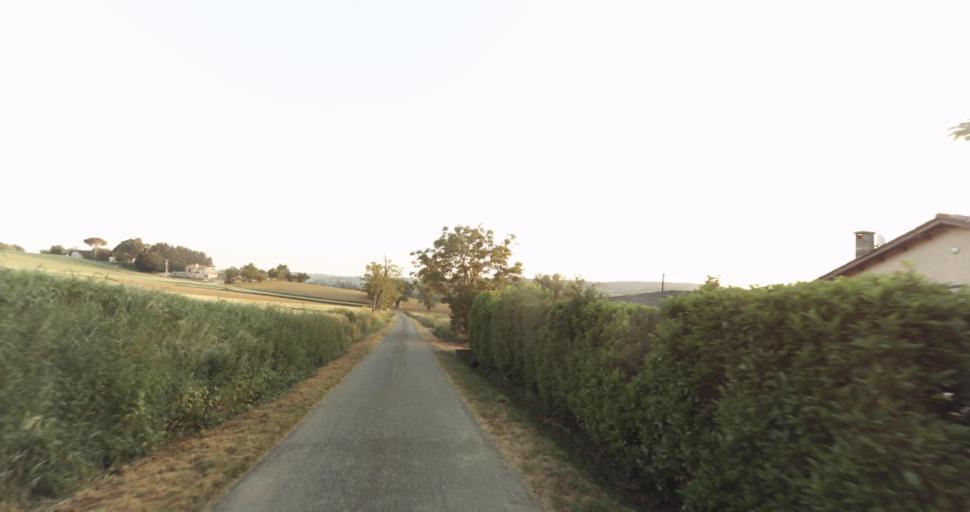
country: FR
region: Midi-Pyrenees
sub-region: Departement du Gers
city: Pujaudran
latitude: 43.6527
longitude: 1.1046
